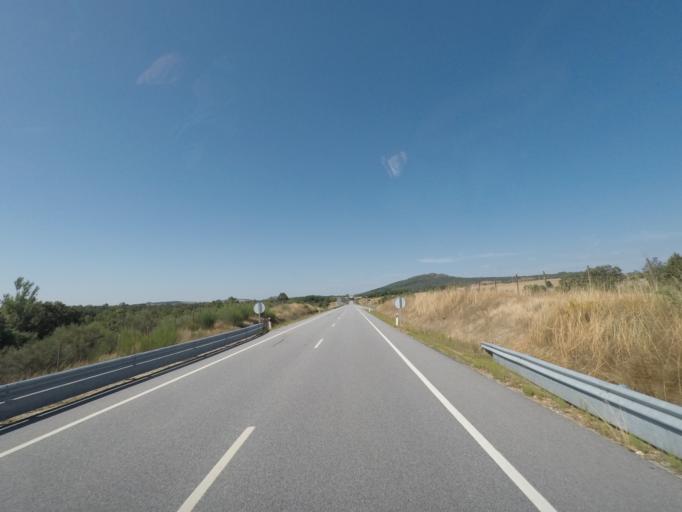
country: PT
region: Braganca
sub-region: Mogadouro
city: Mogadouro
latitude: 41.3550
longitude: -6.5838
